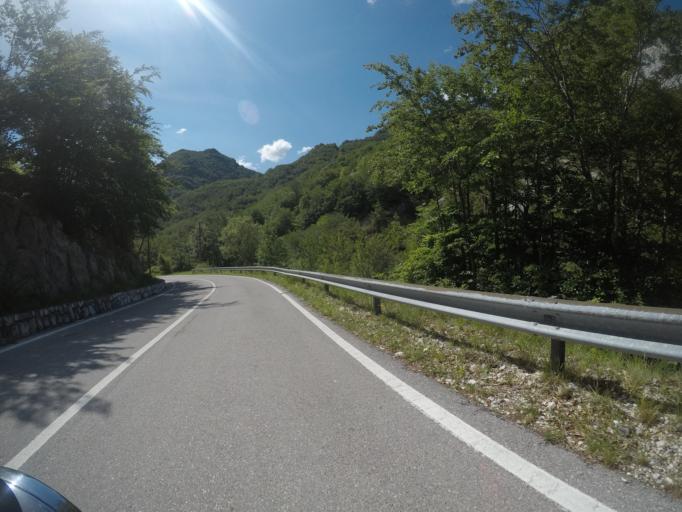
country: IT
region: Tuscany
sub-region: Provincia di Lucca
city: Seravezza
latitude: 44.0594
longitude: 10.2408
